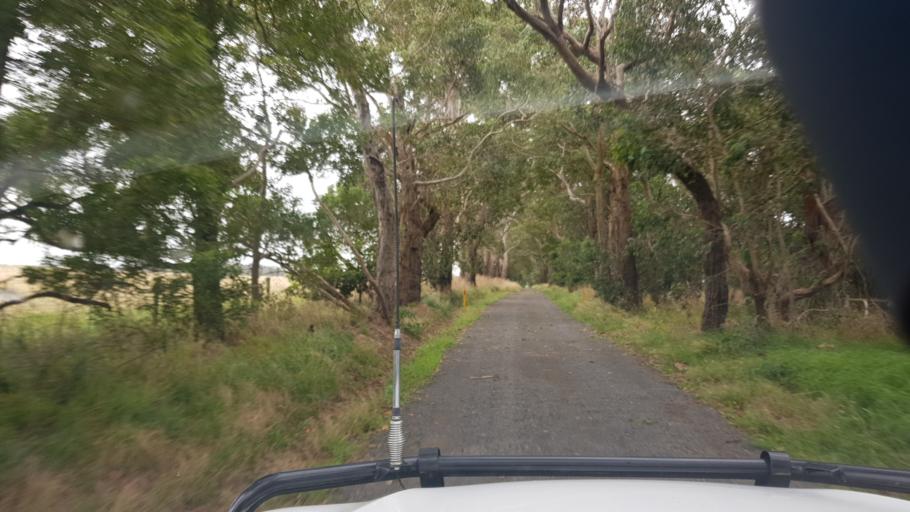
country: AU
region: Victoria
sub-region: Cardinia
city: Bunyip
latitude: -38.1552
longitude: 145.8023
